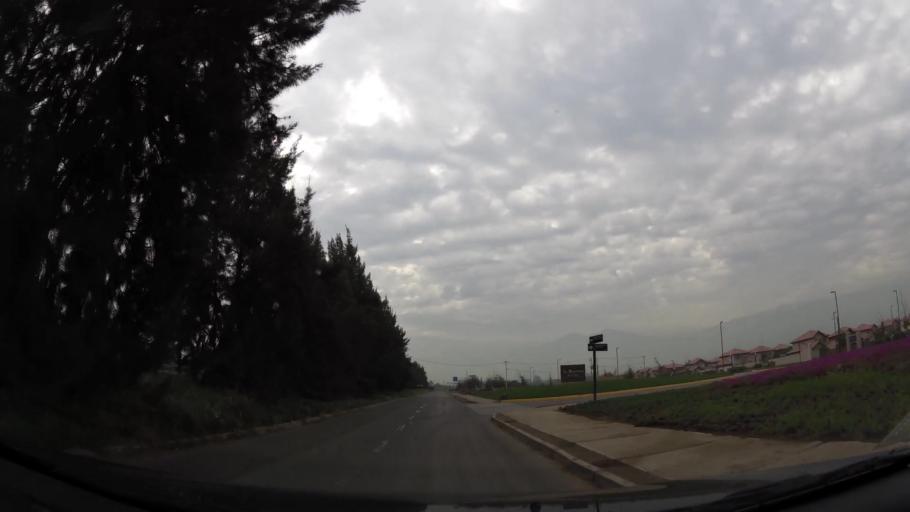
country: CL
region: Santiago Metropolitan
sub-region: Provincia de Chacabuco
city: Chicureo Abajo
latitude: -33.2174
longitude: -70.6753
